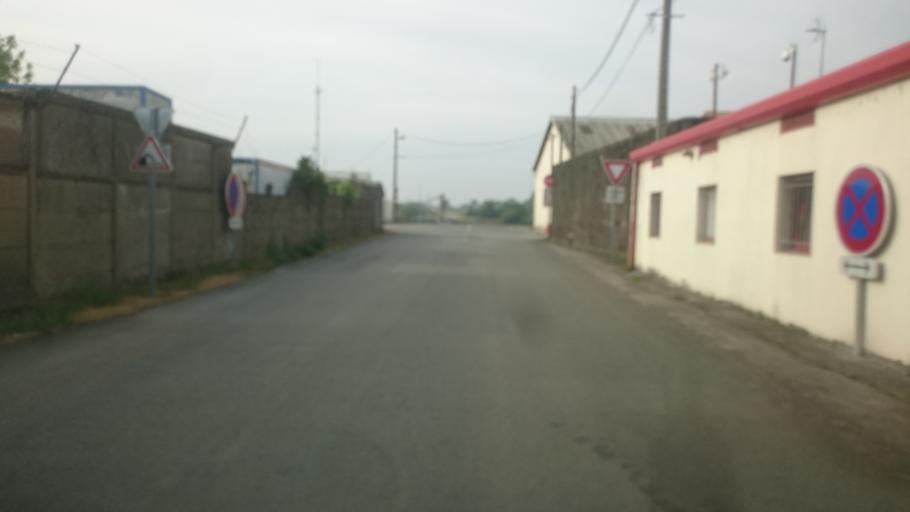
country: FR
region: Pays de la Loire
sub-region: Departement de la Loire-Atlantique
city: Bouguenais
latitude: 47.1946
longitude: -1.6317
